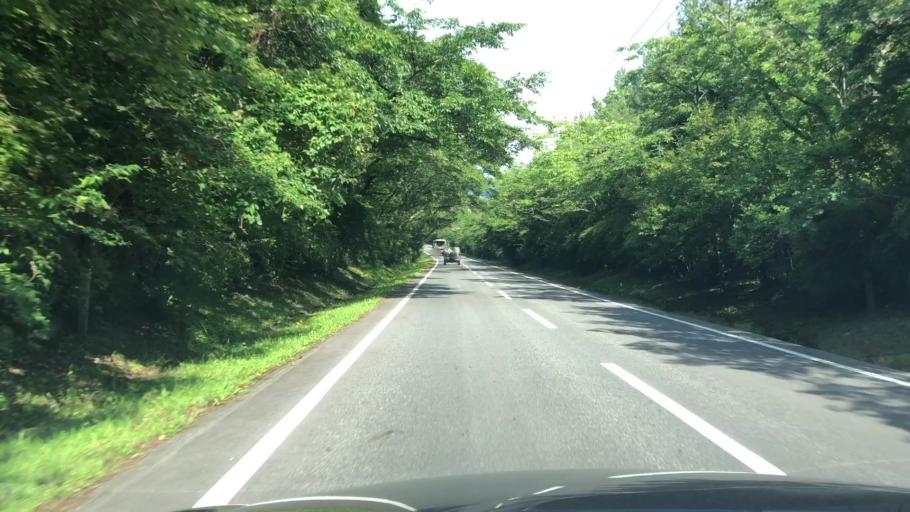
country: JP
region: Shizuoka
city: Gotemba
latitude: 35.3272
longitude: 138.8532
